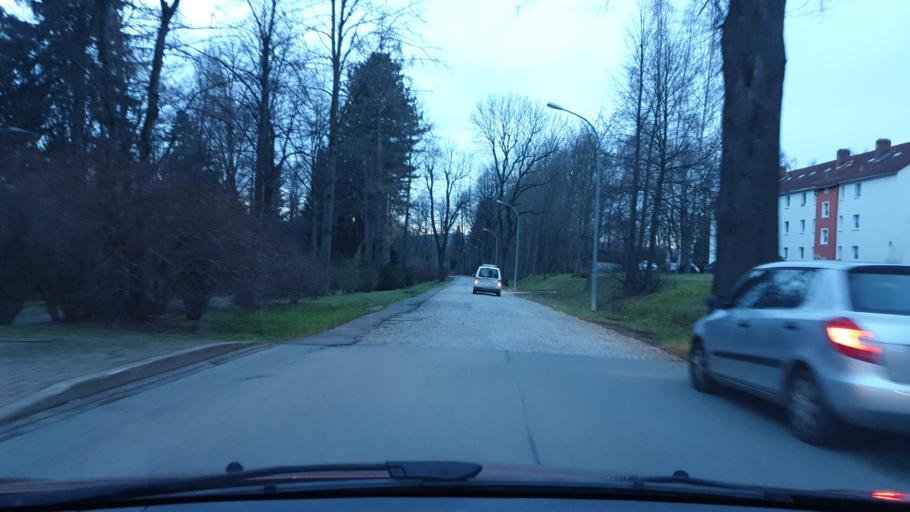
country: DE
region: Saxony
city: Schneeberg
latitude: 50.6060
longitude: 12.6397
